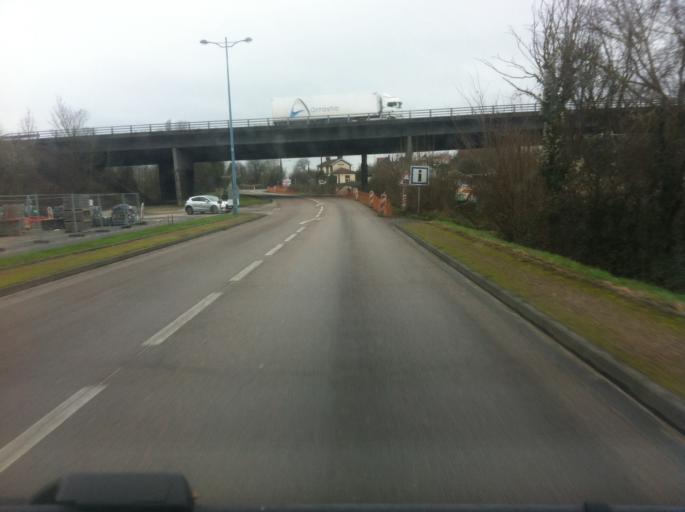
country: FR
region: Haute-Normandie
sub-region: Departement de l'Eure
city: Toutainville
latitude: 49.3634
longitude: 0.4659
